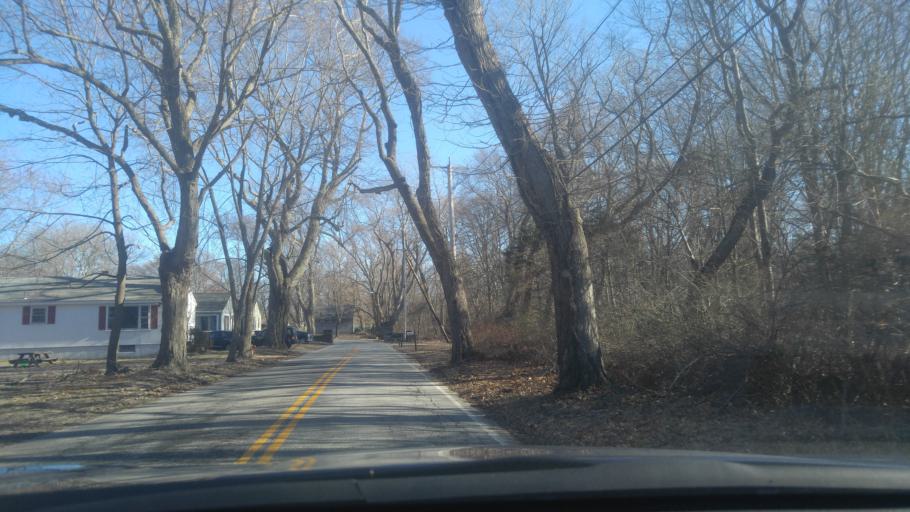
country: US
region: Rhode Island
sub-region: Kent County
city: East Greenwich
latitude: 41.6341
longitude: -71.4155
